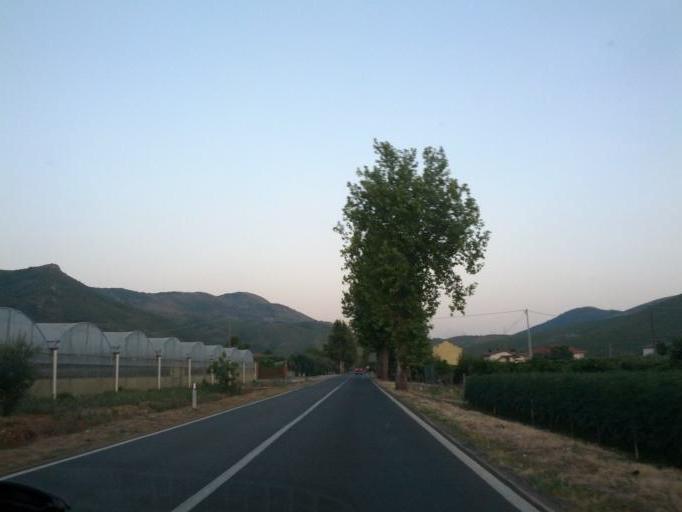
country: IT
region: Latium
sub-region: Provincia di Latina
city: Fondi
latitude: 41.3355
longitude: 13.4598
